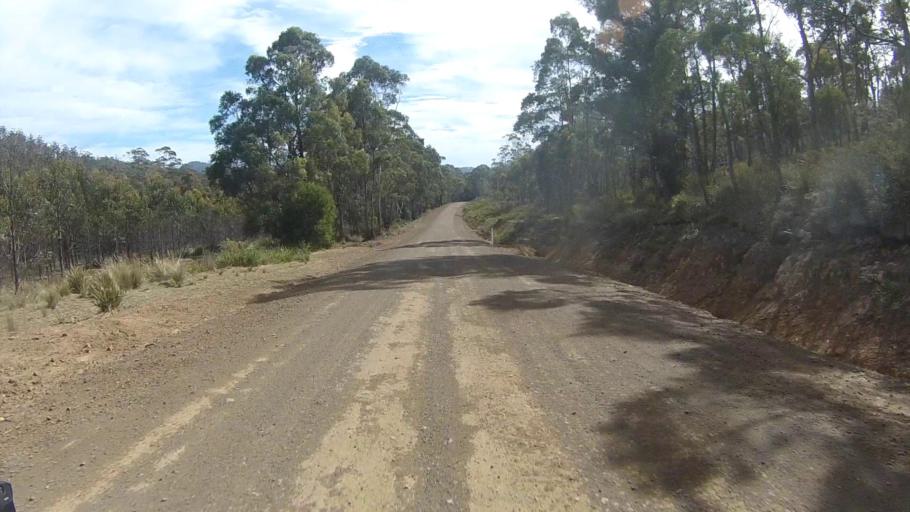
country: AU
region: Tasmania
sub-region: Sorell
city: Sorell
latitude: -42.6674
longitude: 147.8870
